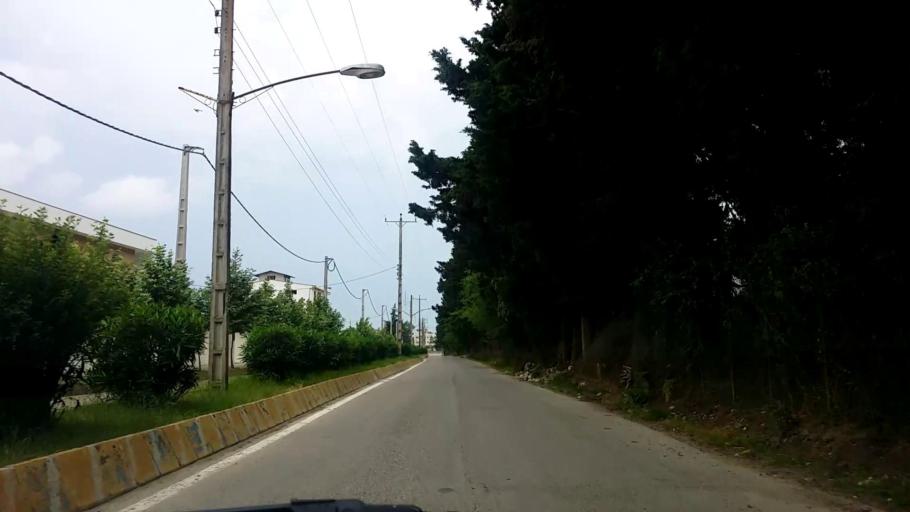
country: IR
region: Mazandaran
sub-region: Nowshahr
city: Nowshahr
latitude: 36.6343
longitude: 51.5026
